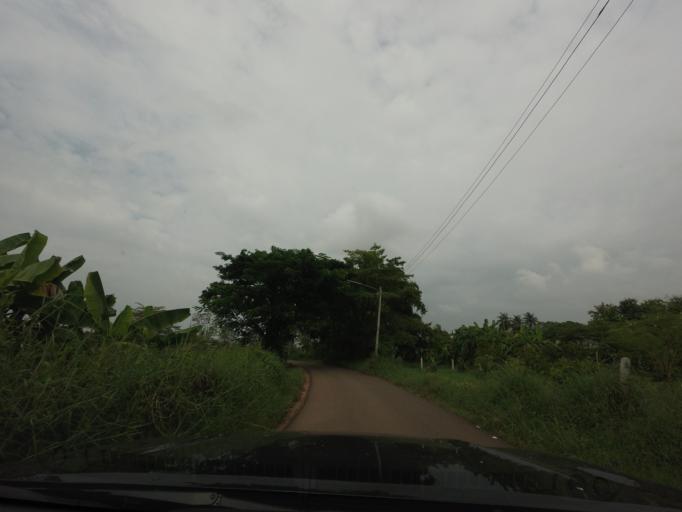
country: TH
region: Nong Khai
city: Nong Khai
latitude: 17.8170
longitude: 102.7076
